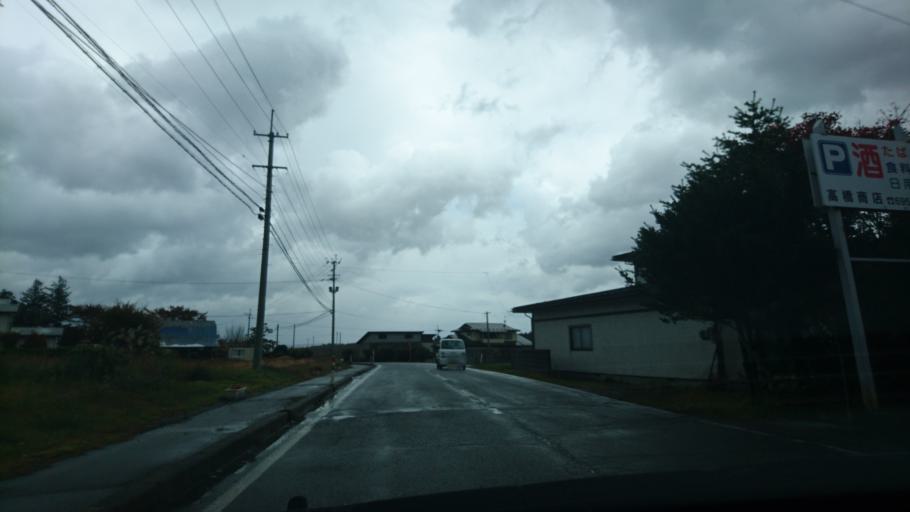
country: JP
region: Iwate
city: Shizukuishi
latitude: 39.6317
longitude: 140.9461
